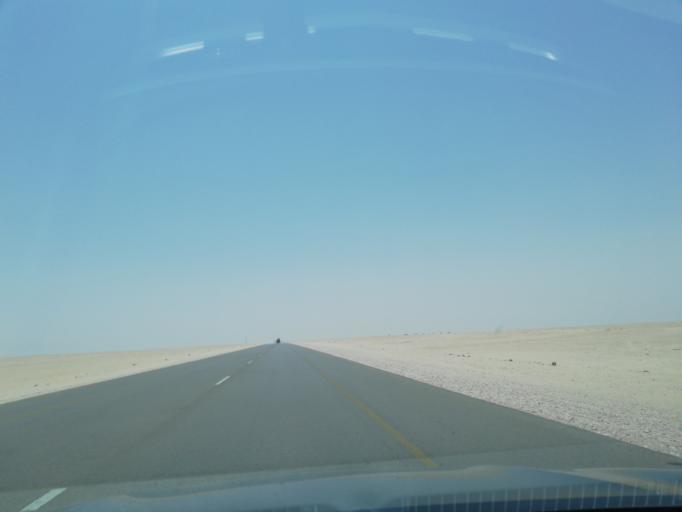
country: OM
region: Al Wusta
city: Hayma'
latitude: 20.1556
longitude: 56.5112
